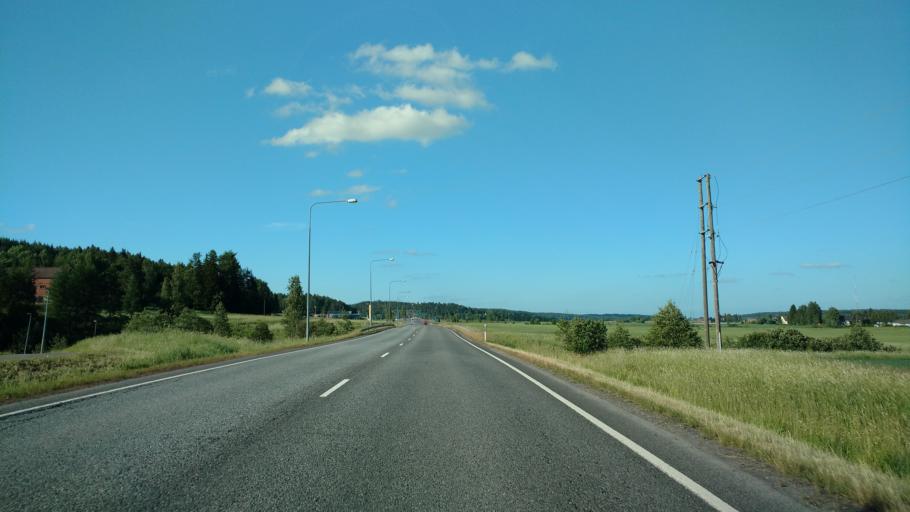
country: FI
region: Varsinais-Suomi
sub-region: Salo
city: Salo
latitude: 60.4106
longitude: 23.1581
